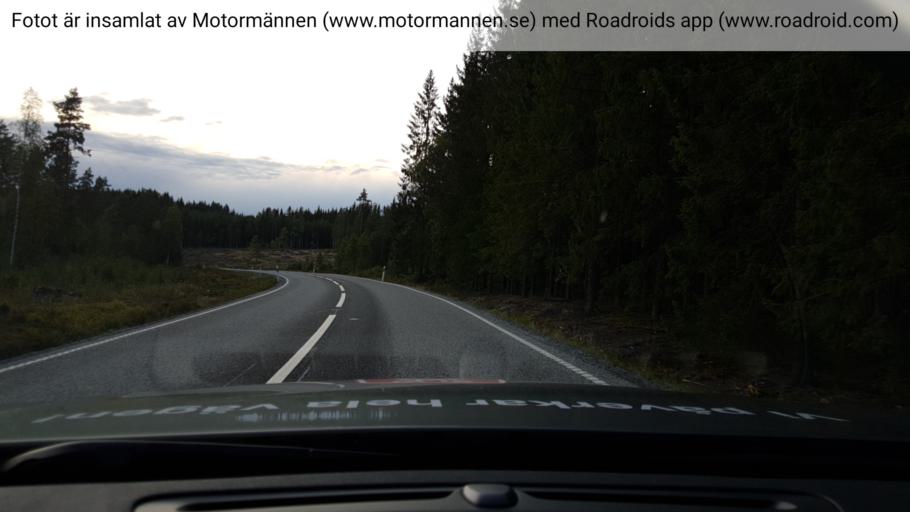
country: SE
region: OErebro
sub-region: Hallefors Kommun
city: Haellefors
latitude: 59.8107
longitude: 14.6928
